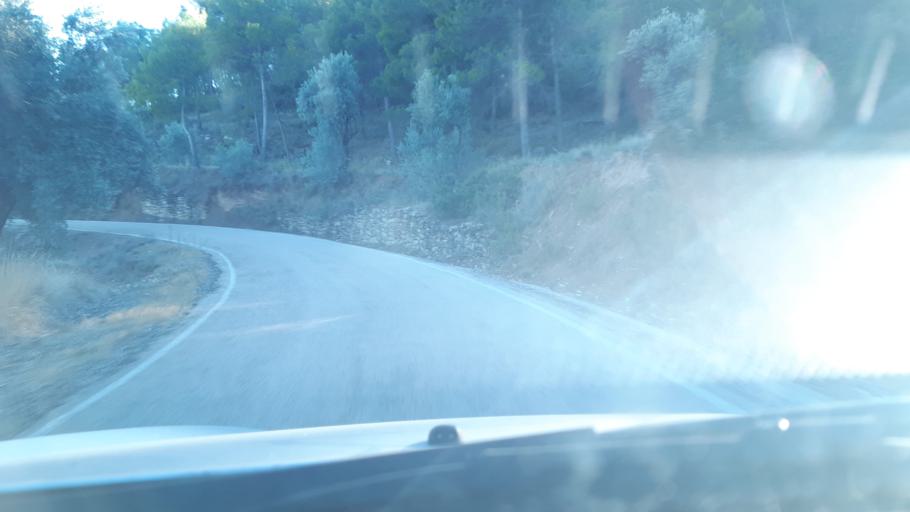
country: ES
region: Aragon
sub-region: Provincia de Teruel
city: Fornoles
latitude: 40.9073
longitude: -0.0135
